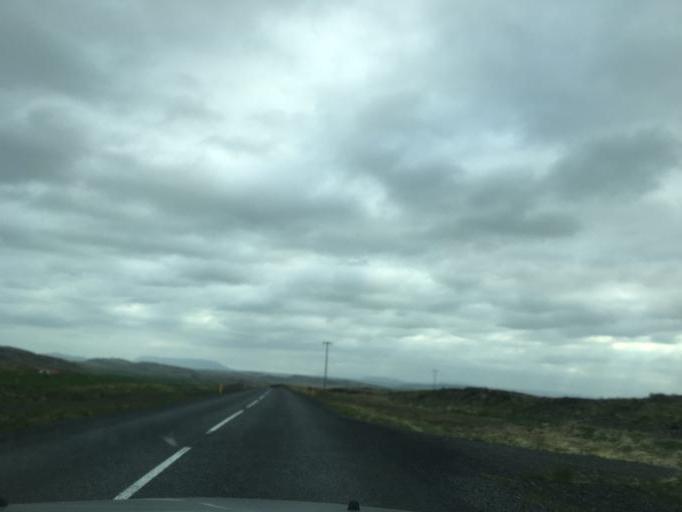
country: IS
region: South
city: Vestmannaeyjar
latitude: 64.2367
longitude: -20.2324
